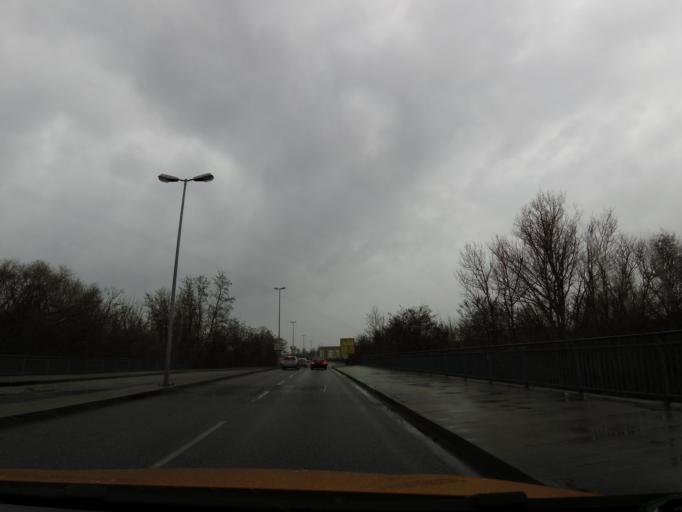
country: DE
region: Brandenburg
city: Brandenburg an der Havel
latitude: 52.4048
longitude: 12.5382
